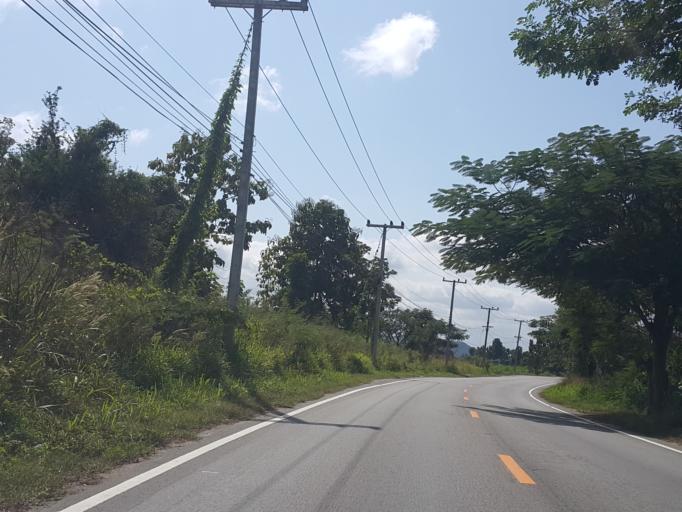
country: TH
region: Chiang Mai
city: San Kamphaeng
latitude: 18.7150
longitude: 99.1723
